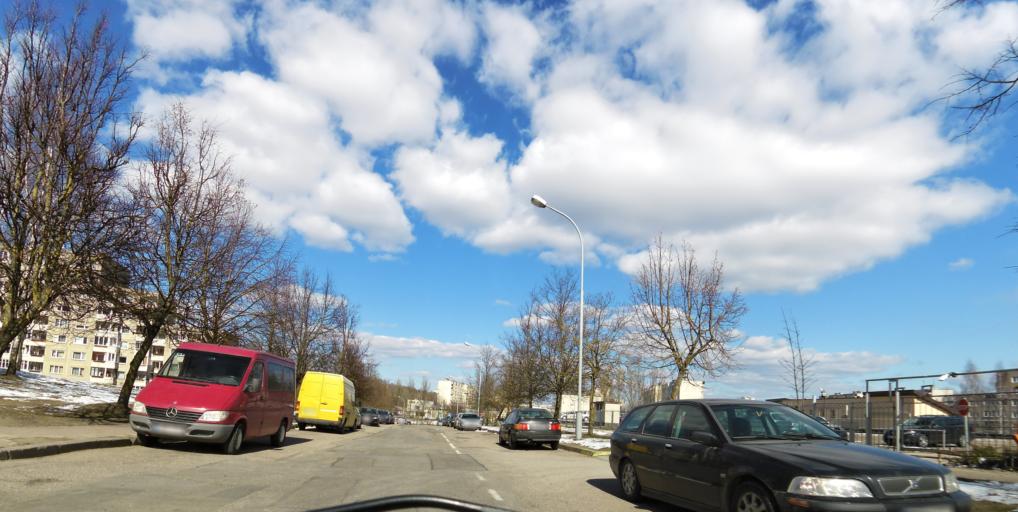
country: LT
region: Vilnius County
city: Pasilaiciai
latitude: 54.7271
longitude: 25.2258
